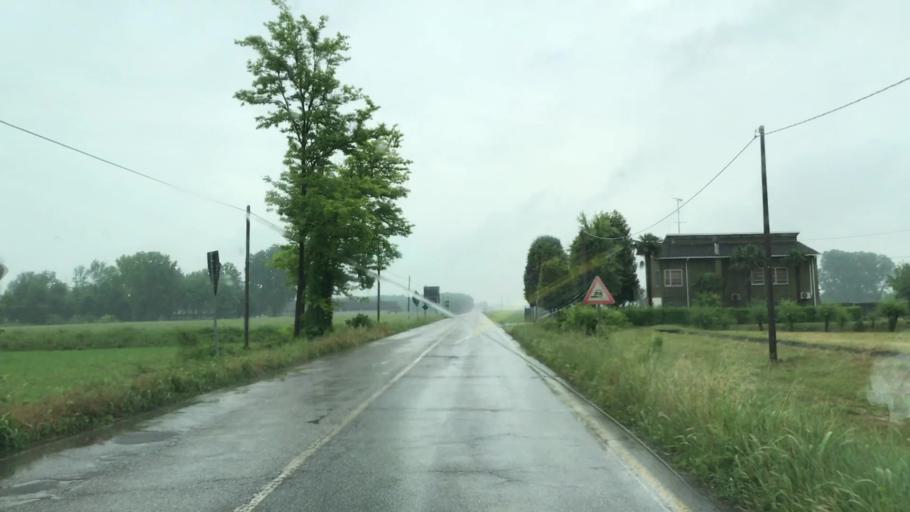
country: IT
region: Lombardy
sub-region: Provincia di Mantova
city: Gazzuolo
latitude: 45.0614
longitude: 10.5773
